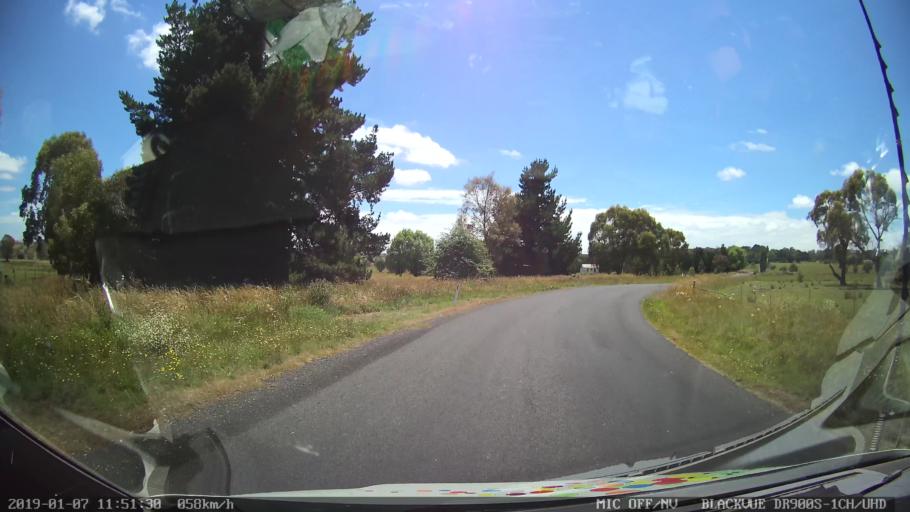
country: AU
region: New South Wales
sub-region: Guyra
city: Guyra
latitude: -30.3076
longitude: 151.6456
